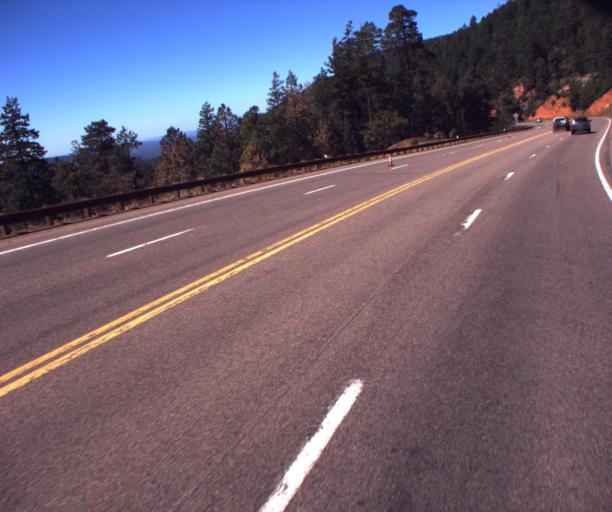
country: US
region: Arizona
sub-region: Gila County
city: Star Valley
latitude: 34.3035
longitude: -110.9196
